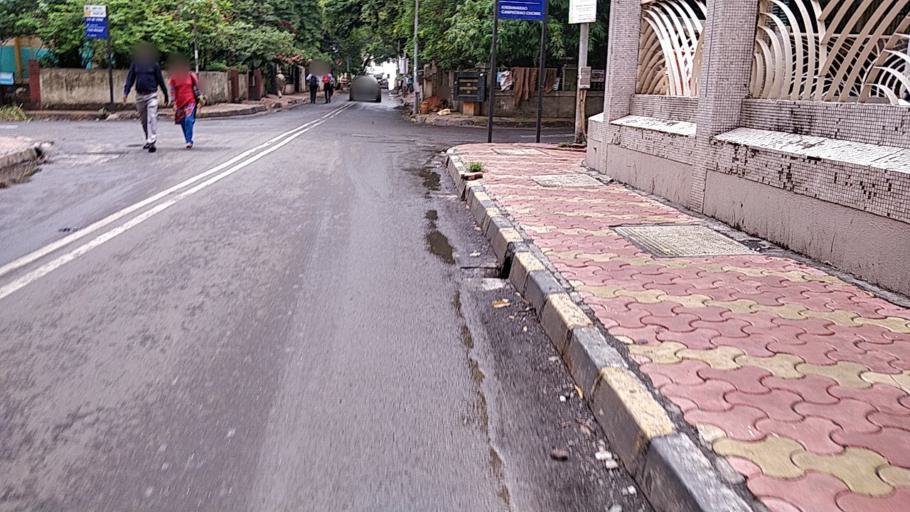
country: IN
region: Maharashtra
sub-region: Mumbai Suburban
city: Mumbai
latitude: 19.0701
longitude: 72.8357
